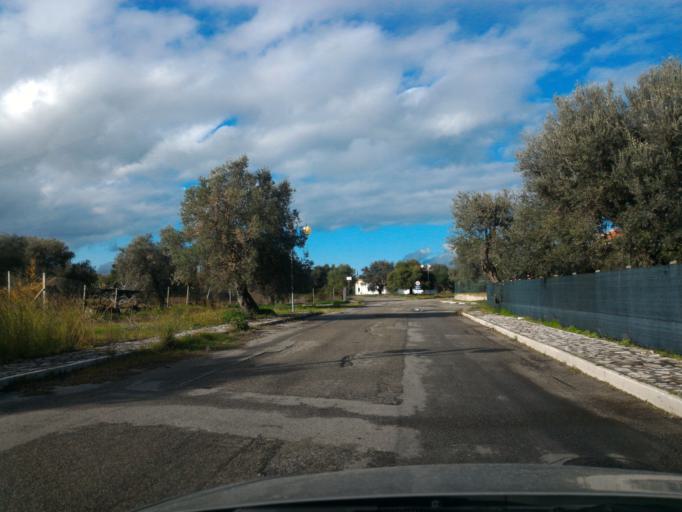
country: IT
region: Calabria
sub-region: Provincia di Crotone
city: Torretta
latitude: 39.4581
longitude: 17.0347
